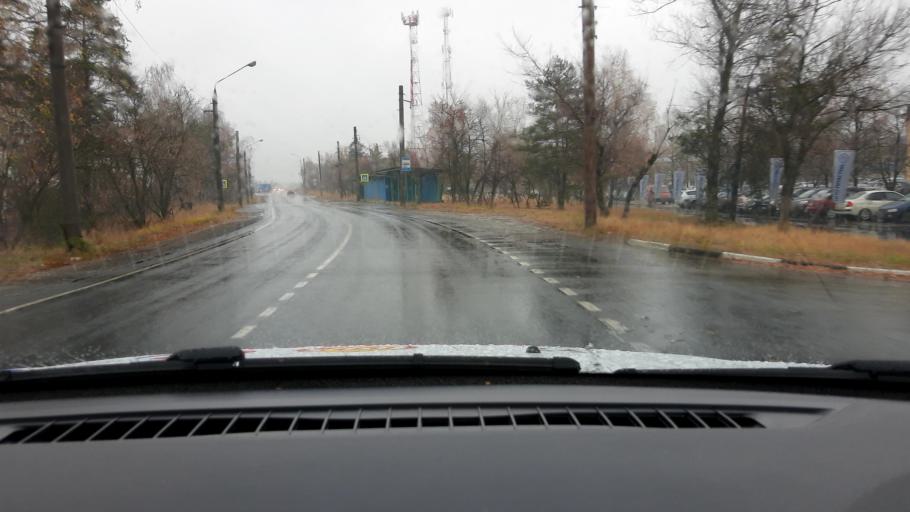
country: RU
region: Nizjnij Novgorod
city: Babino
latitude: 56.2890
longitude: 43.5999
